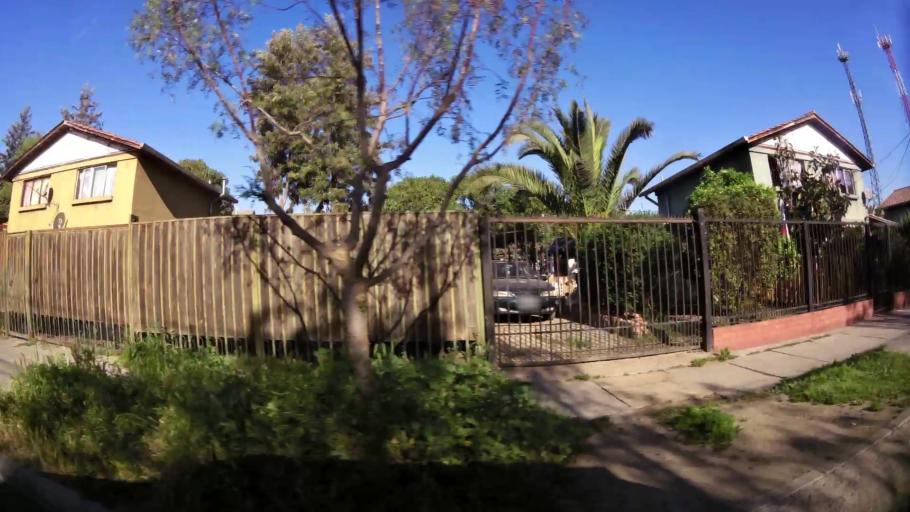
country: CL
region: Santiago Metropolitan
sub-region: Provincia de Talagante
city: Penaflor
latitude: -33.6038
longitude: -70.8596
